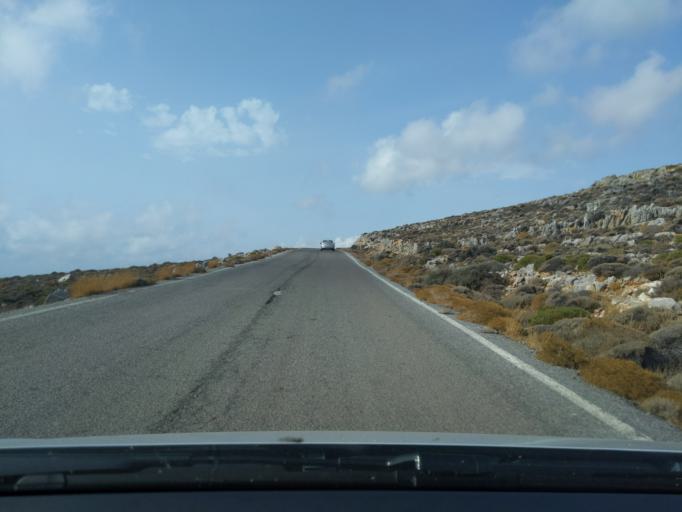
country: GR
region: Crete
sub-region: Nomos Lasithiou
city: Palekastro
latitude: 35.0853
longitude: 26.2635
